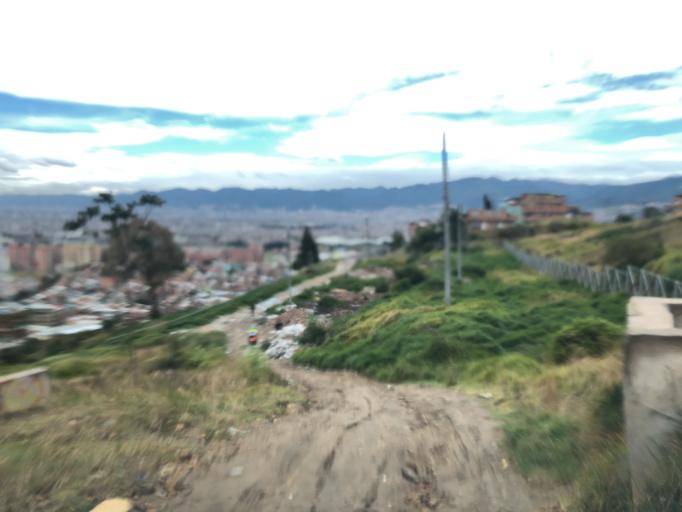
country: CO
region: Cundinamarca
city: Soacha
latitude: 4.5781
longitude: -74.1728
